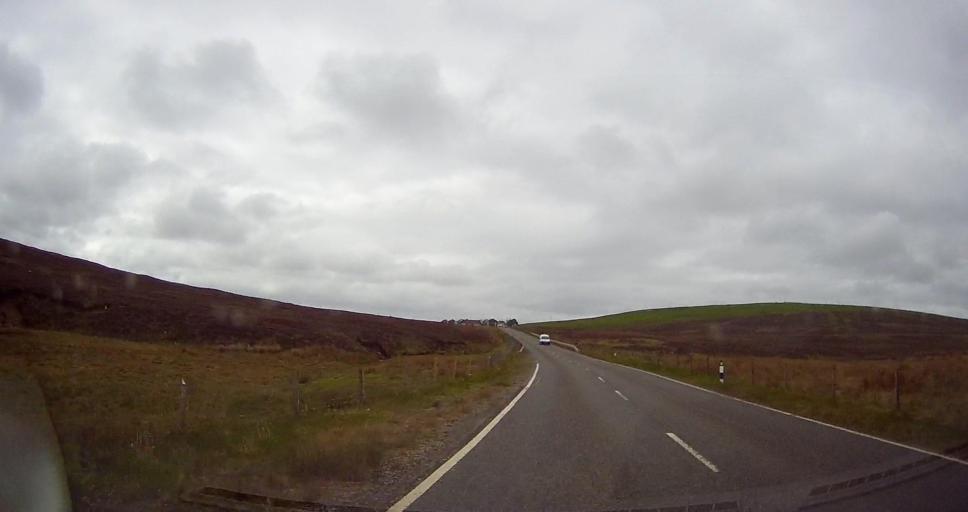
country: GB
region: Scotland
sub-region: Shetland Islands
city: Lerwick
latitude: 60.2519
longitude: -1.3874
